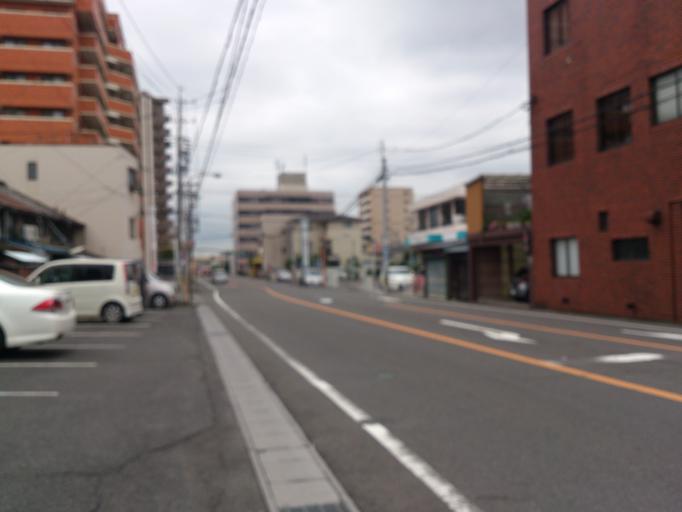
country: JP
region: Gifu
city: Ogaki
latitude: 35.3685
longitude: 136.6212
